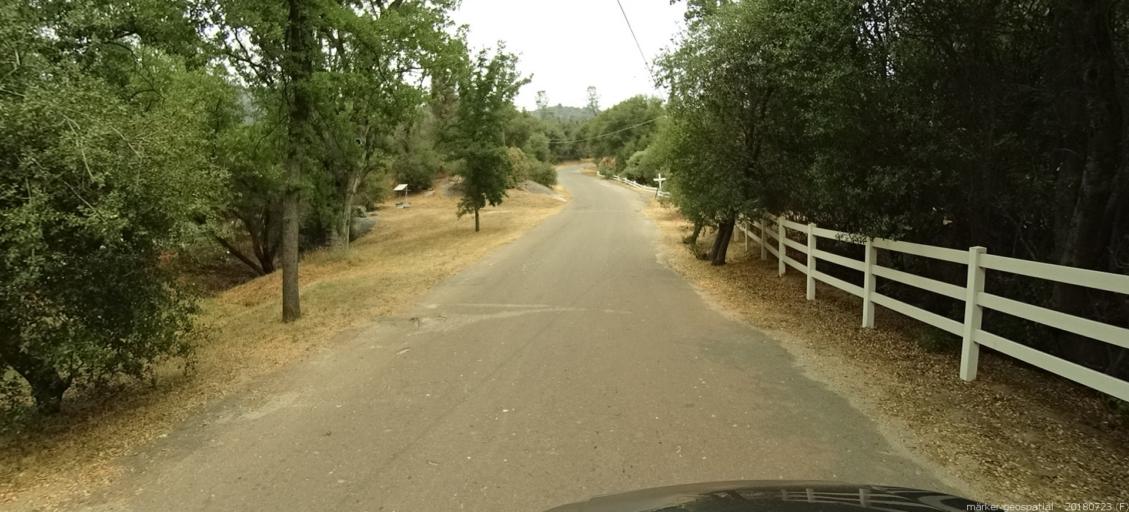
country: US
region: California
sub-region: Madera County
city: Oakhurst
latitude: 37.3578
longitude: -119.6386
